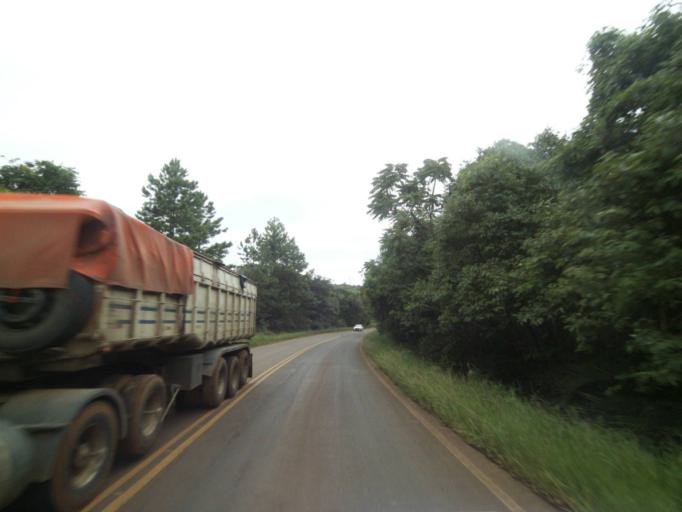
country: BR
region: Parana
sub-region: Pitanga
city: Pitanga
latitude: -24.9194
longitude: -51.8702
